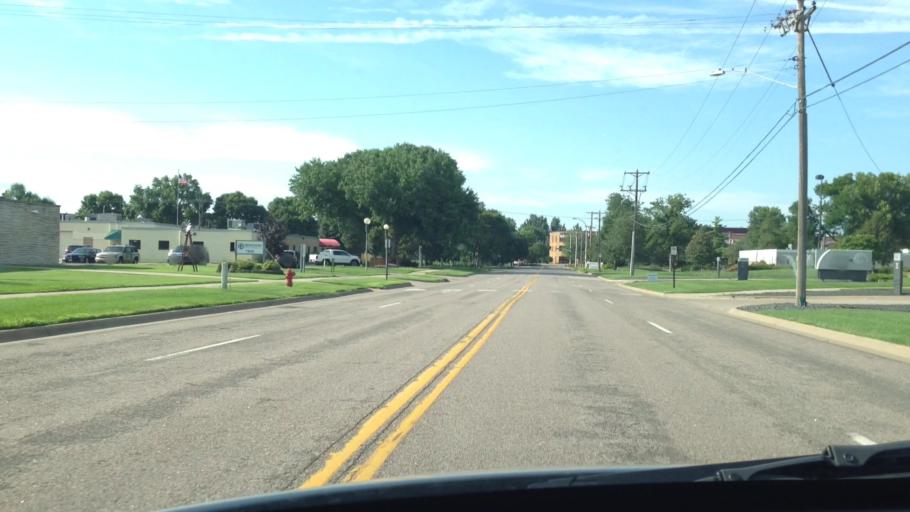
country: US
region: Minnesota
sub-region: Hennepin County
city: Edina
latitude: 44.8604
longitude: -93.3457
